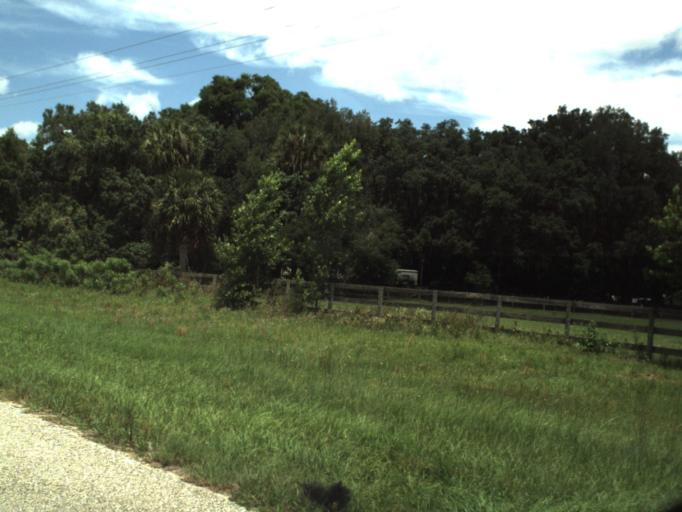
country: US
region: Florida
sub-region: Marion County
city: Citra
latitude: 29.3770
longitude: -82.1763
